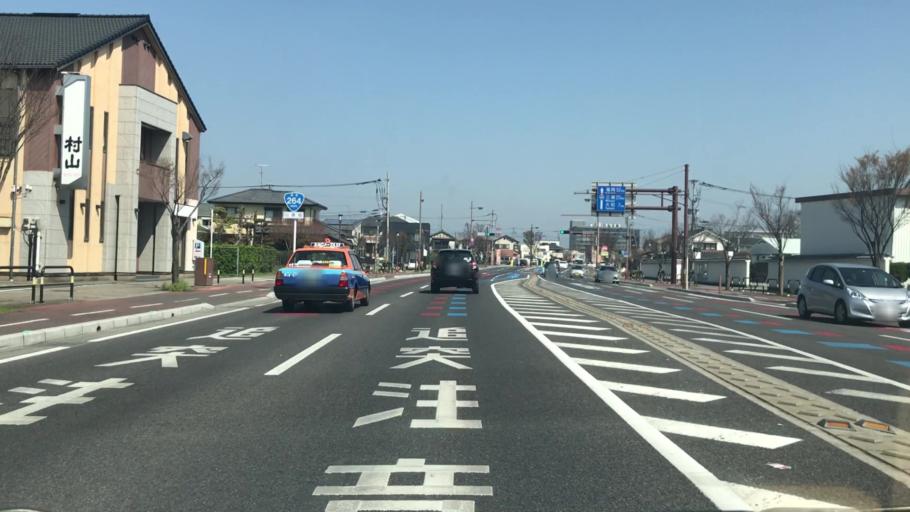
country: JP
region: Saga Prefecture
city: Saga-shi
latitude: 33.2509
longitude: 130.2923
